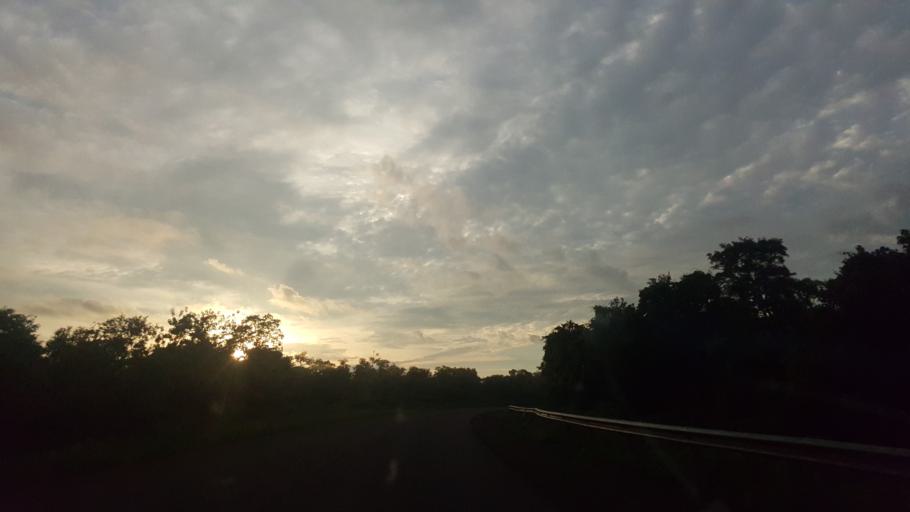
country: AR
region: Misiones
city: Dos de Mayo
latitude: -26.9272
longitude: -54.7221
